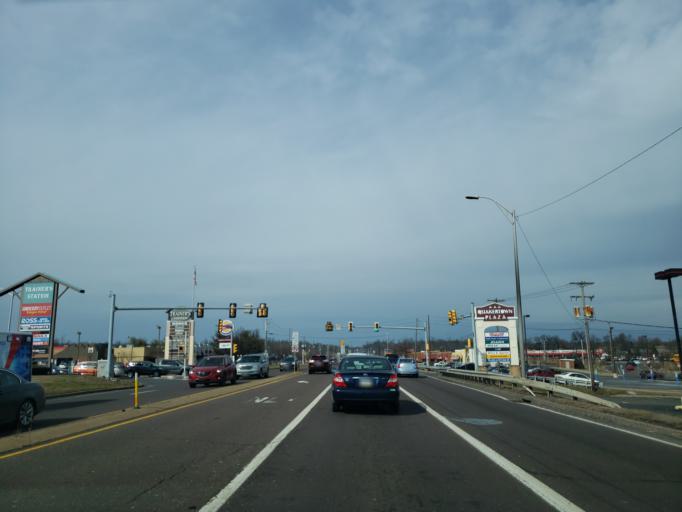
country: US
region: Pennsylvania
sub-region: Bucks County
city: Quakertown
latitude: 40.4456
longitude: -75.3595
